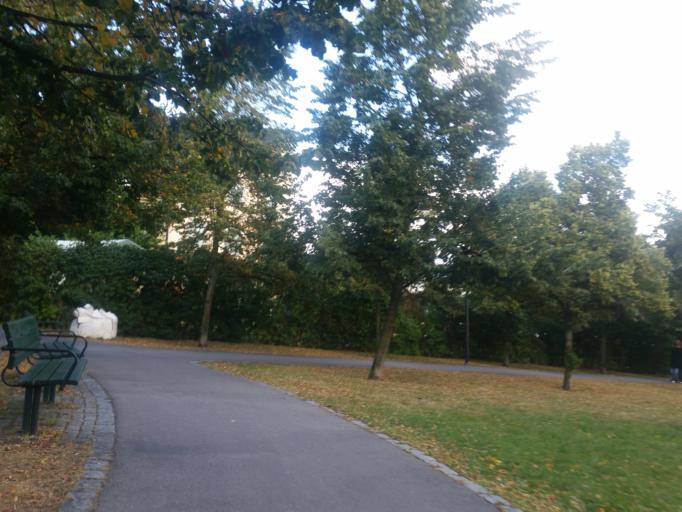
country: SE
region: Stockholm
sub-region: Stockholms Kommun
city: OEstermalm
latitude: 59.3083
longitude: 18.0959
